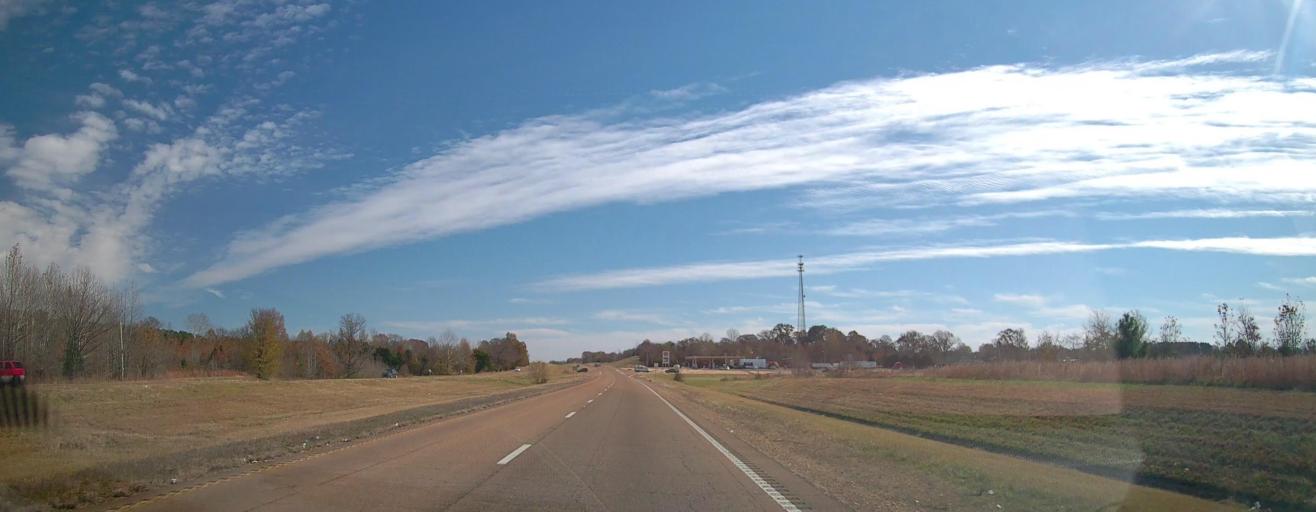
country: US
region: Tennessee
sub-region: Fayette County
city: Piperton
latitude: 34.9613
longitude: -89.5321
